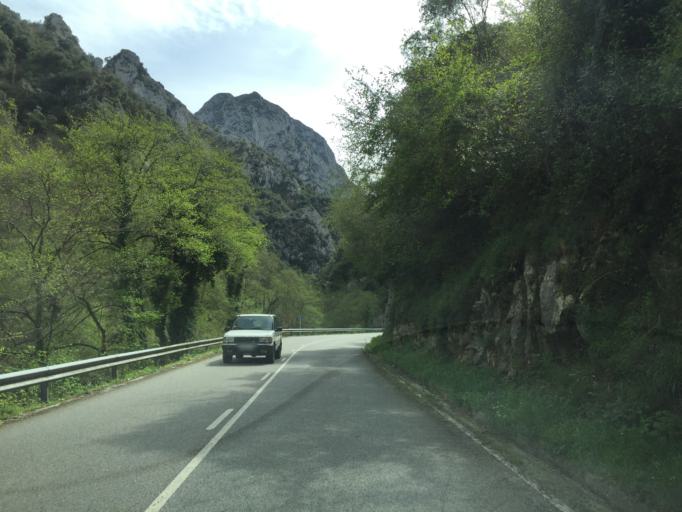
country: ES
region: Asturias
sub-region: Province of Asturias
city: Proaza
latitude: 43.2473
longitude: -6.0244
